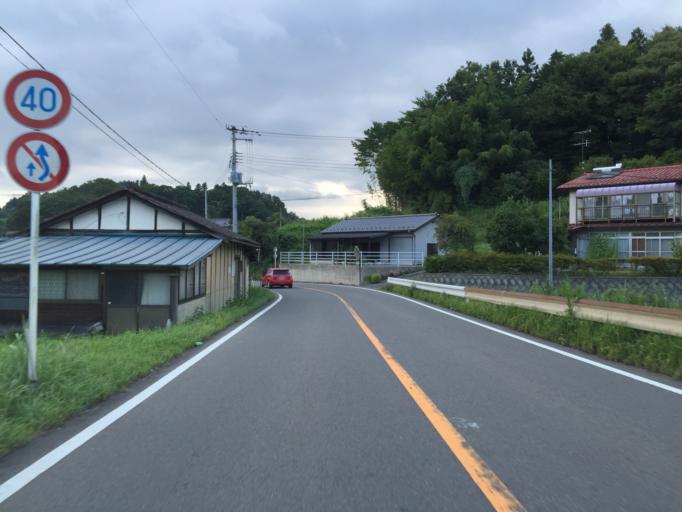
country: JP
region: Fukushima
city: Fukushima-shi
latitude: 37.6660
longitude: 140.5174
